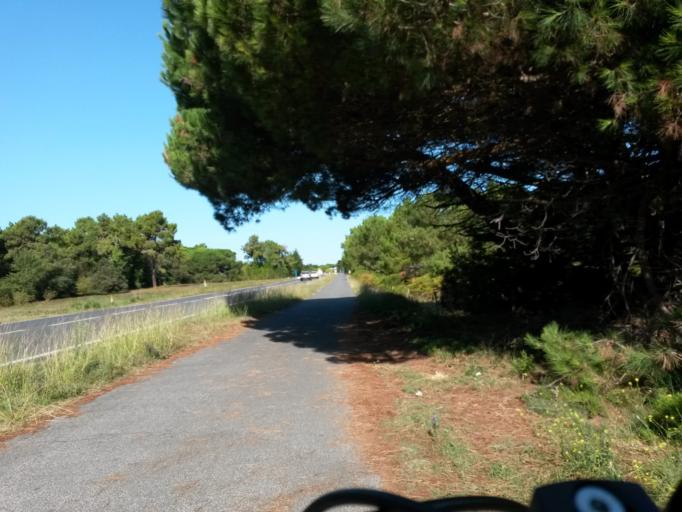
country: FR
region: Poitou-Charentes
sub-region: Departement de la Charente-Maritime
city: La Flotte
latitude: 46.1668
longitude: -1.3579
